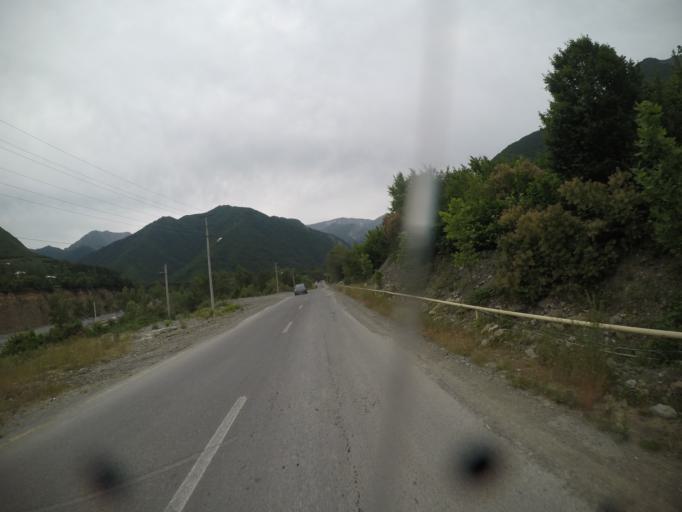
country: AZ
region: Shaki City
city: Sheki
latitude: 41.2510
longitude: 47.2053
